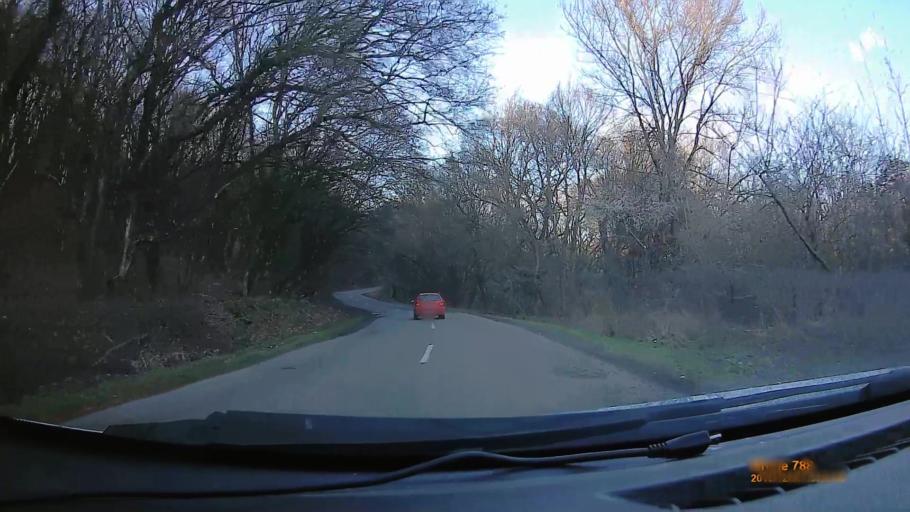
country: HU
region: Heves
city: Sirok
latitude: 47.8919
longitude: 20.1890
